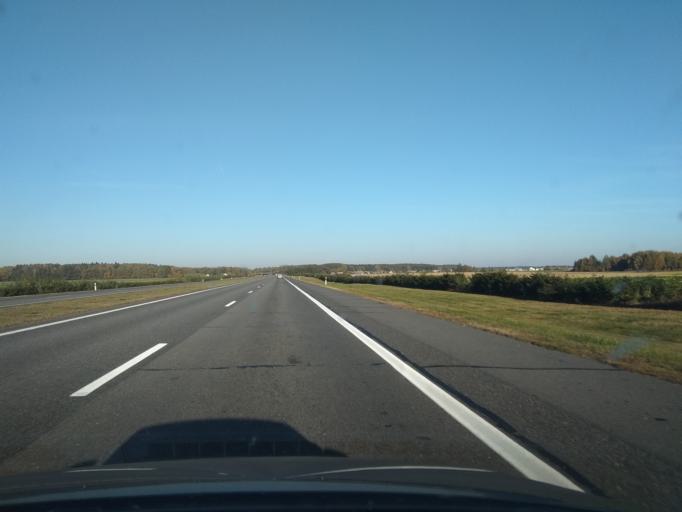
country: BY
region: Brest
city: Ivatsevichy
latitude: 52.6698
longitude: 25.3034
